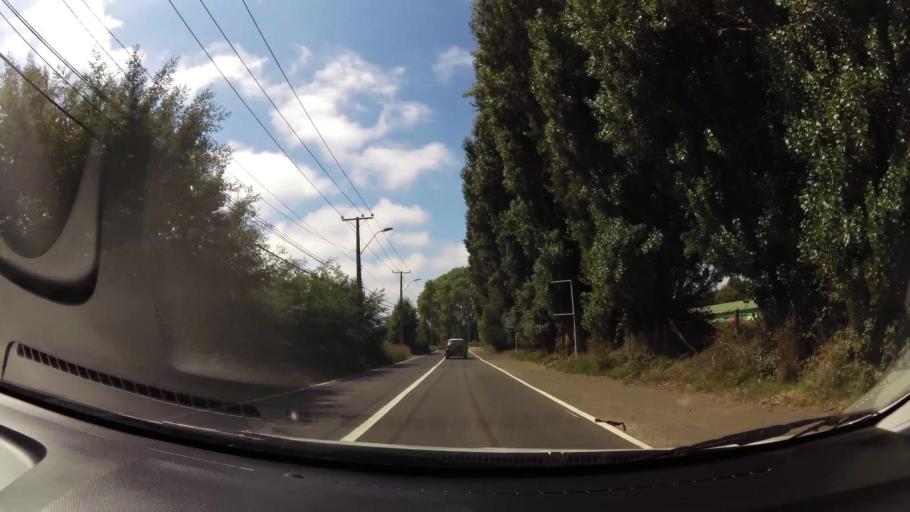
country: CL
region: Biobio
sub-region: Provincia de Concepcion
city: Concepcion
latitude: -36.7789
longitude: -73.0571
